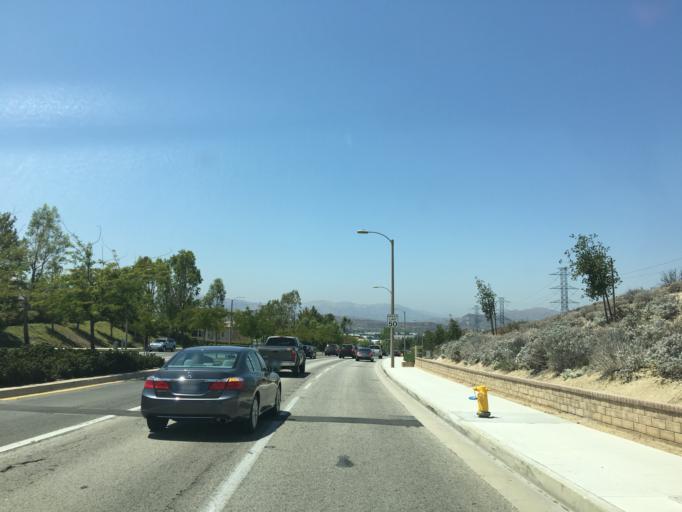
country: US
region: California
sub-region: Los Angeles County
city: Valencia
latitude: 34.4475
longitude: -118.5686
